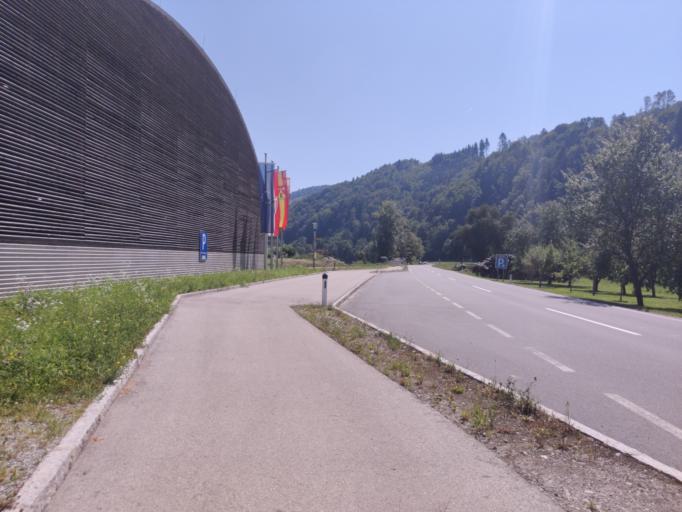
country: AT
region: Upper Austria
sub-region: Politischer Bezirk Rohrbach
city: Pfarrkirchen im Muehlkreis
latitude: 48.4714
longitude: 13.7736
